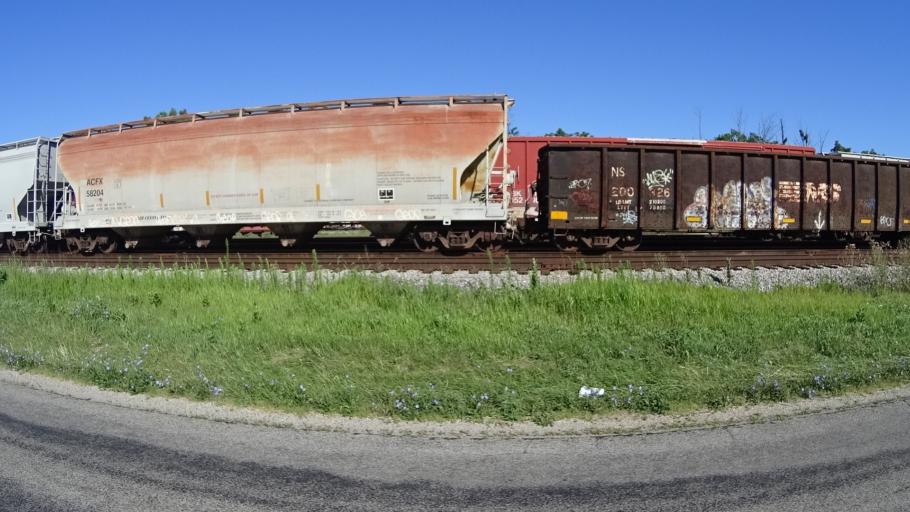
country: US
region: Ohio
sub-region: Erie County
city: Sandusky
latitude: 41.4036
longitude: -82.7477
